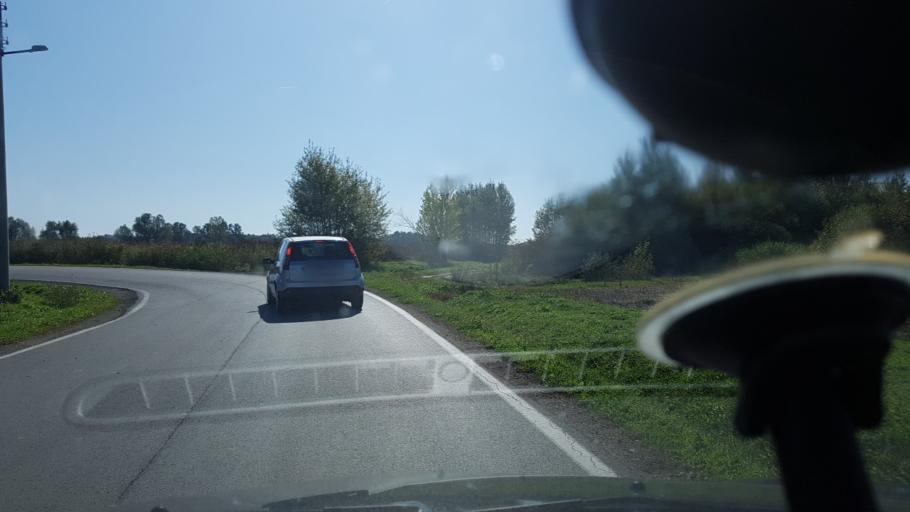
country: HR
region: Zagrebacka
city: Lupoglav
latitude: 45.7082
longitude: 16.3356
